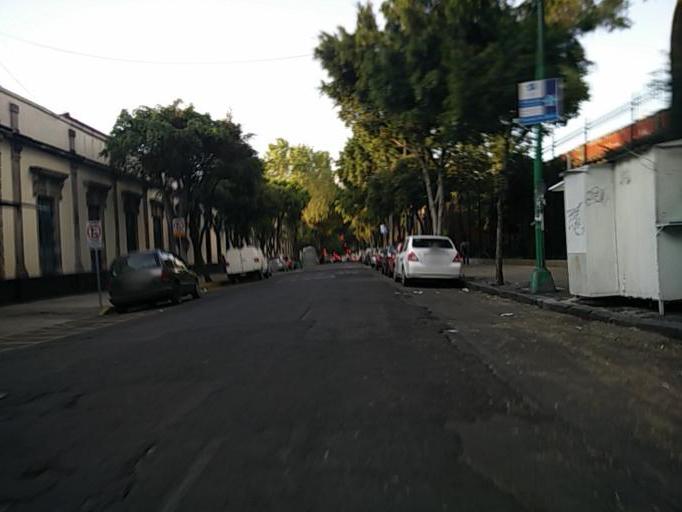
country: MX
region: Mexico City
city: Cuauhtemoc
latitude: 19.4282
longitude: -99.1506
